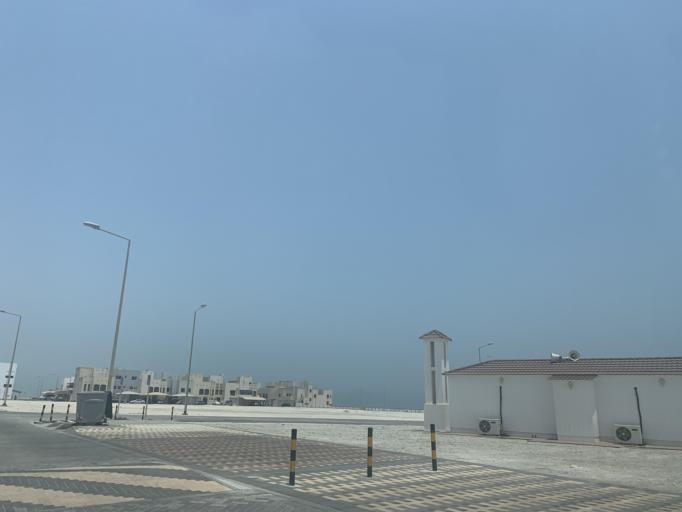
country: BH
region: Muharraq
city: Al Hadd
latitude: 26.2330
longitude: 50.6780
